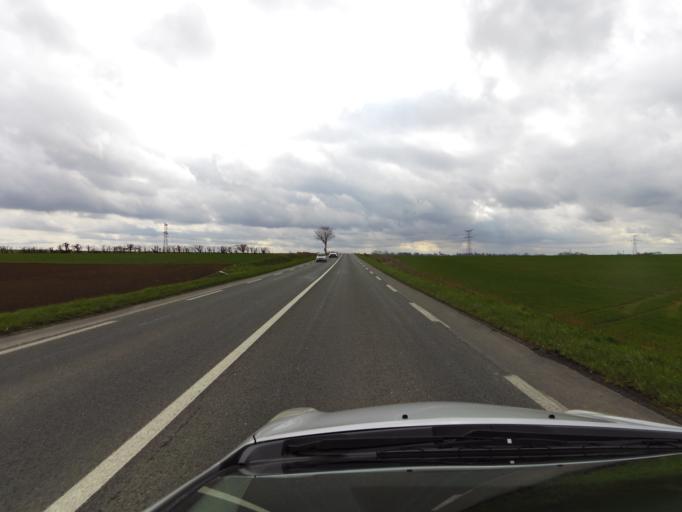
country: FR
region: Nord-Pas-de-Calais
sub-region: Departement du Pas-de-Calais
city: Beaurains
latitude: 50.2507
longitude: 2.7920
